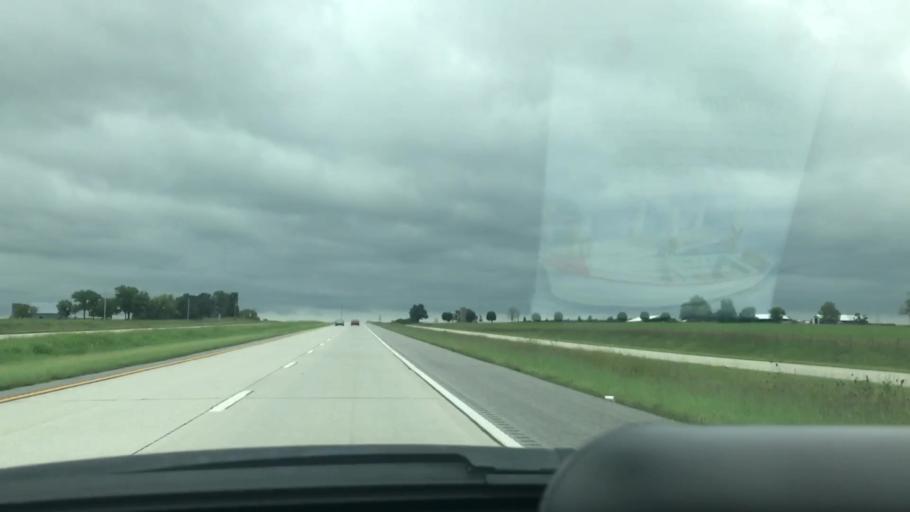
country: US
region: Missouri
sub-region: Greene County
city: Fair Grove
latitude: 37.4322
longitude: -93.1447
